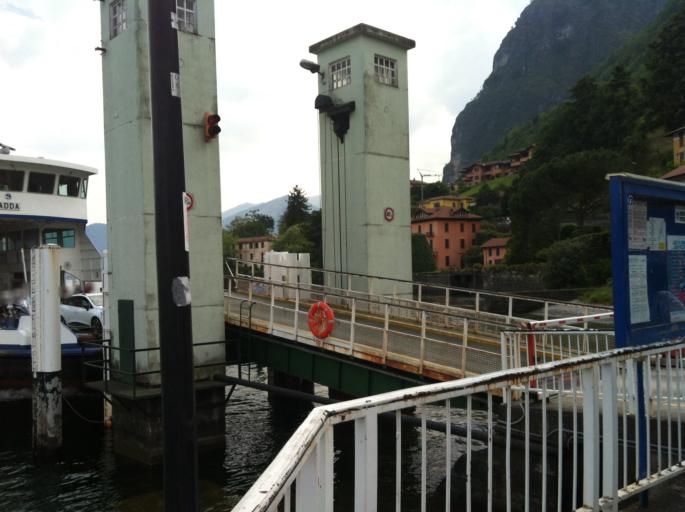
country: IT
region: Lombardy
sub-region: Provincia di Como
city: Menaggio
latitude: 46.0171
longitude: 9.2370
